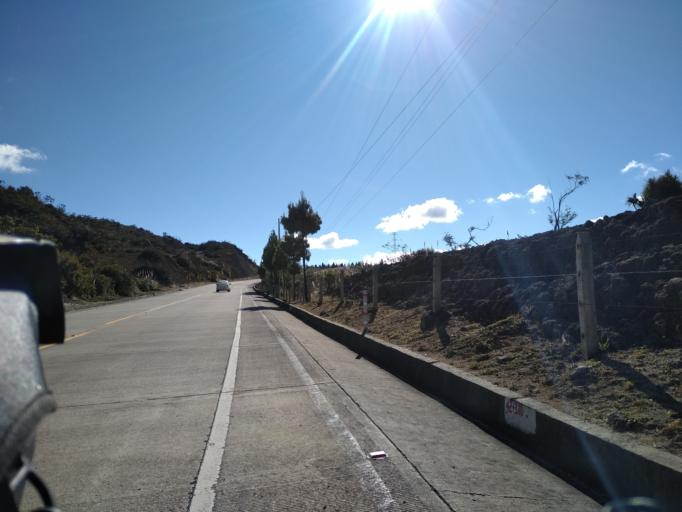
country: EC
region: Azuay
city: Cuenca
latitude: -3.3075
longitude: -79.1264
